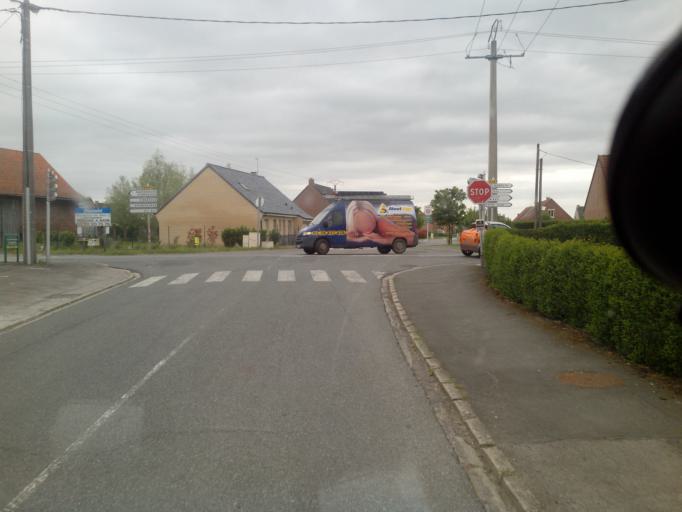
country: FR
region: Nord-Pas-de-Calais
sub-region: Departement du Nord
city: Vieux-Berquin
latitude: 50.6975
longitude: 2.6425
